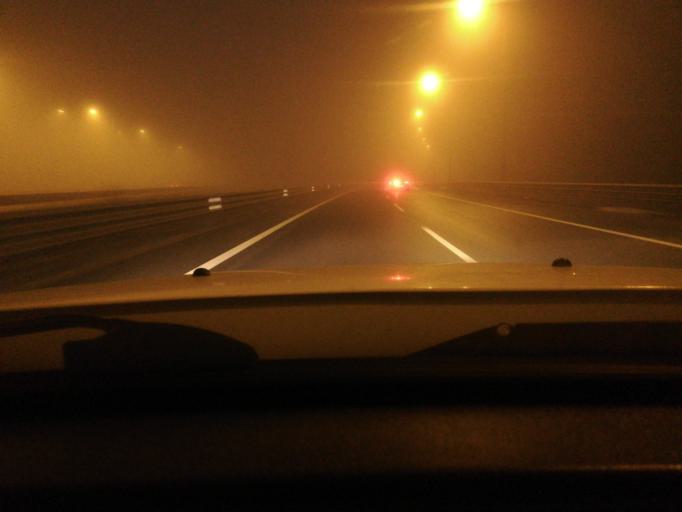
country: TR
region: Istanbul
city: Sultanbeyli
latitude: 40.9760
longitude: 29.3271
